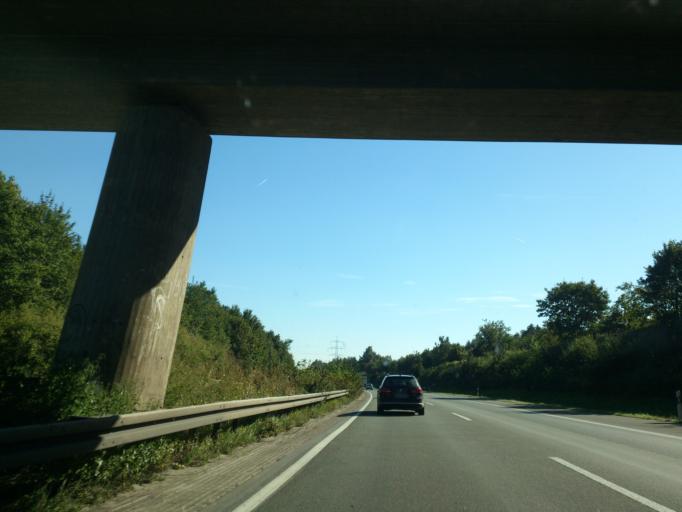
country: DE
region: North Rhine-Westphalia
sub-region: Regierungsbezirk Detmold
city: Oerlinghausen
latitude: 51.9063
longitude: 8.6235
